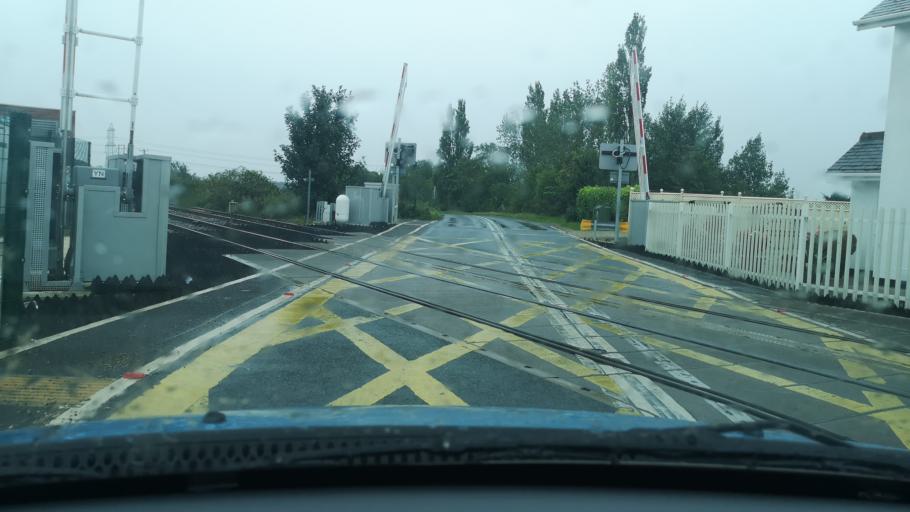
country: GB
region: England
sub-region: Doncaster
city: Norton
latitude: 53.6784
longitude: -1.2114
